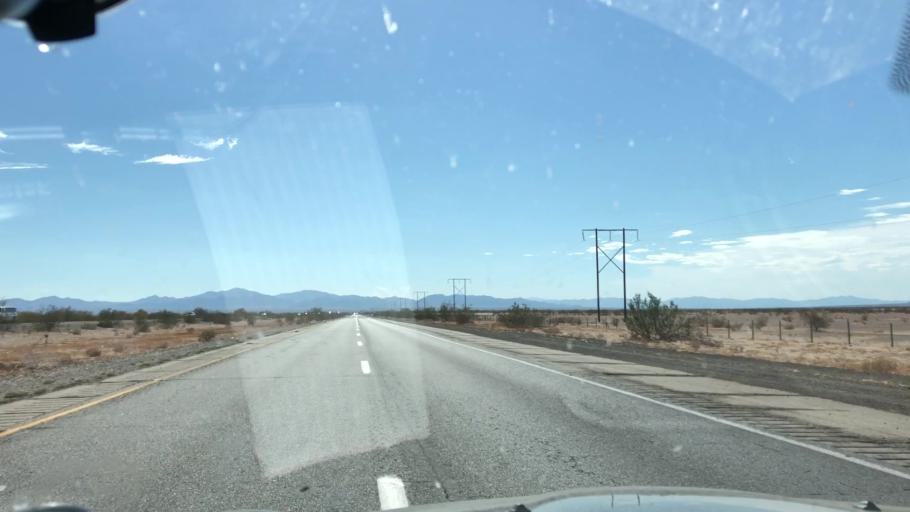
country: US
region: California
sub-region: Riverside County
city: Mesa Verde
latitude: 33.6062
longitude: -114.9469
